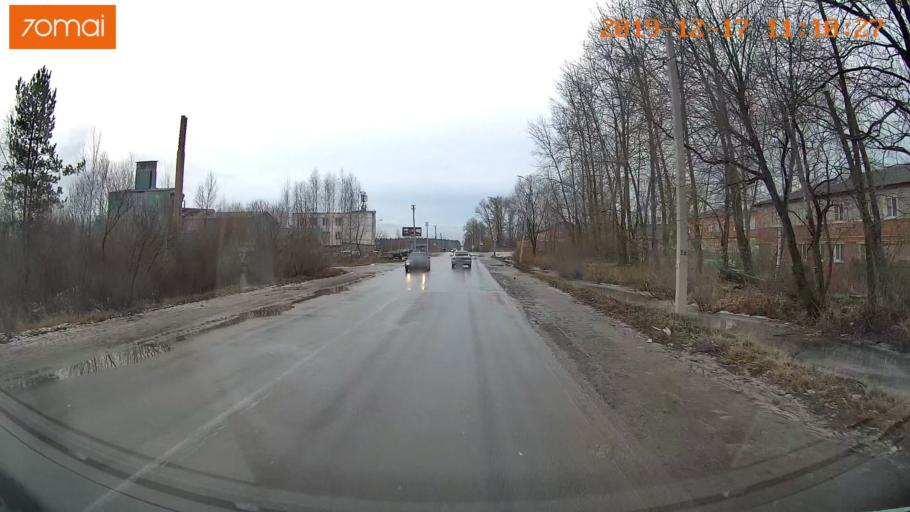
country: RU
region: Vladimir
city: Gus'-Khrustal'nyy
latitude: 55.5927
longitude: 40.6414
